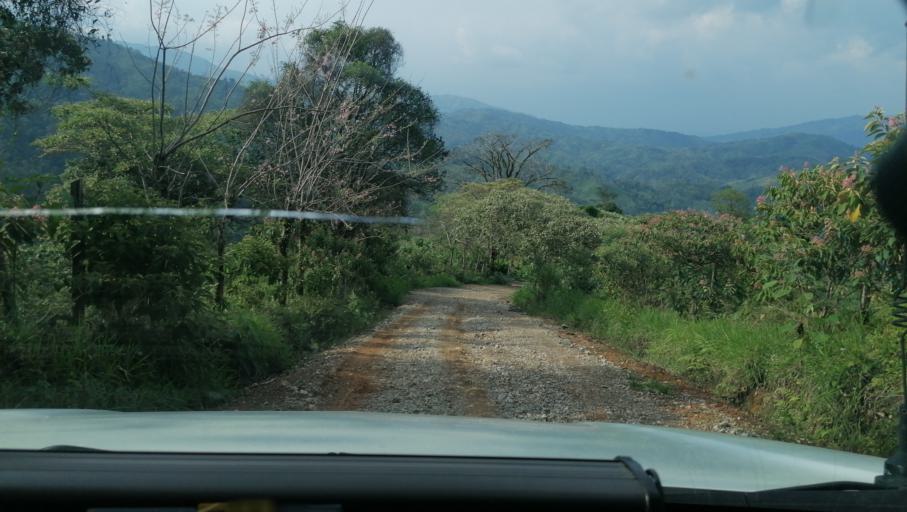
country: MX
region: Chiapas
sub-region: Tapilula
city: San Francisco Jacona
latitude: 17.3202
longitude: -93.0994
